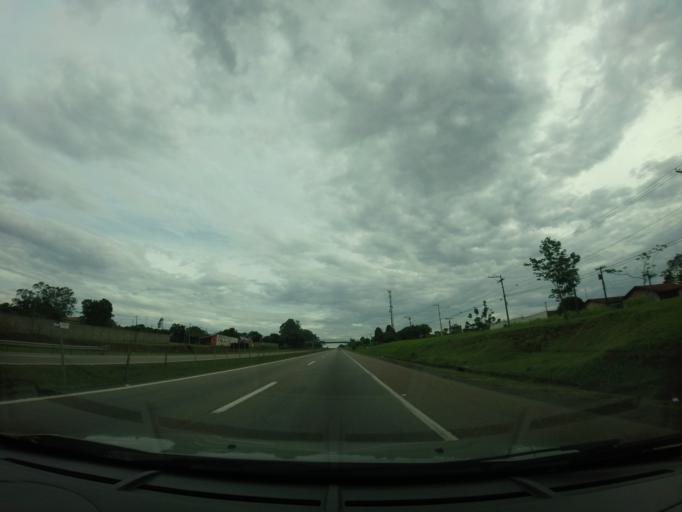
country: BR
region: Sao Paulo
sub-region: Piracicaba
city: Piracicaba
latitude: -22.7541
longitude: -47.5979
